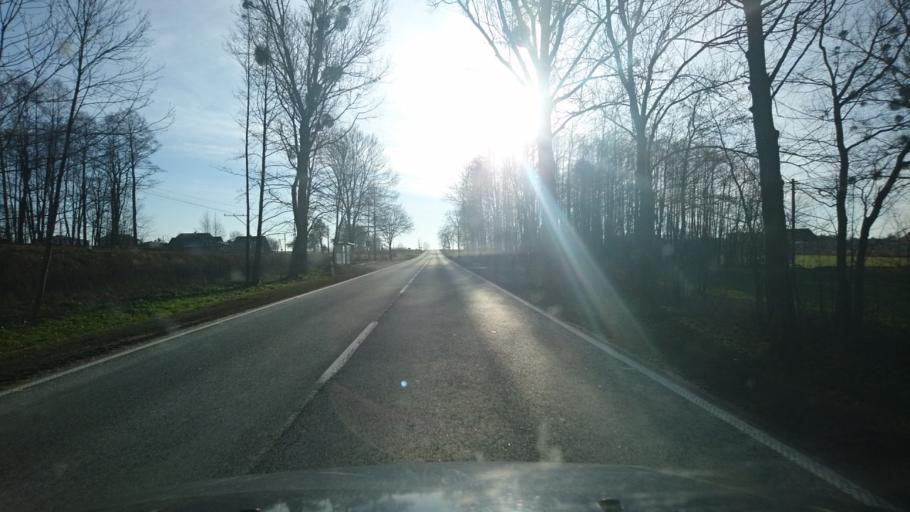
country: PL
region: Opole Voivodeship
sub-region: Powiat oleski
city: Dalachow
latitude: 51.0664
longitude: 18.6009
